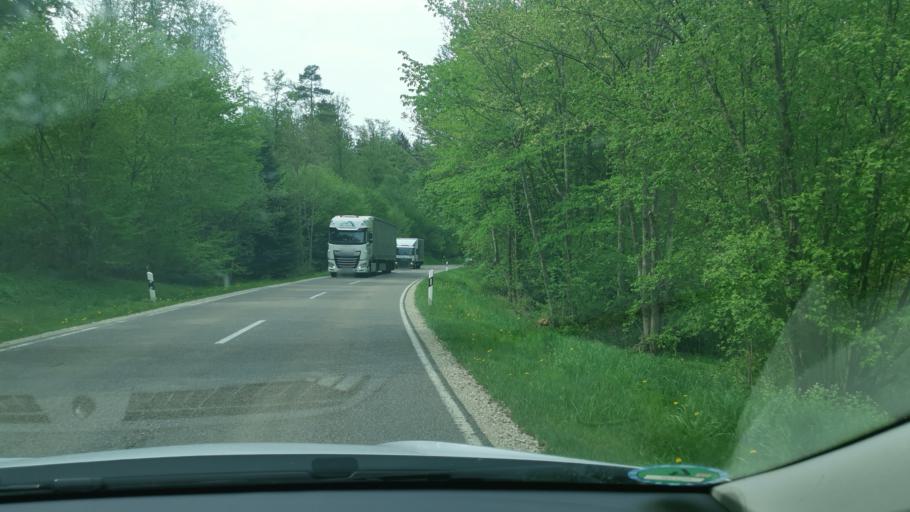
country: DE
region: Bavaria
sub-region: Swabia
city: Schiltberg
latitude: 48.4424
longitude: 11.2617
